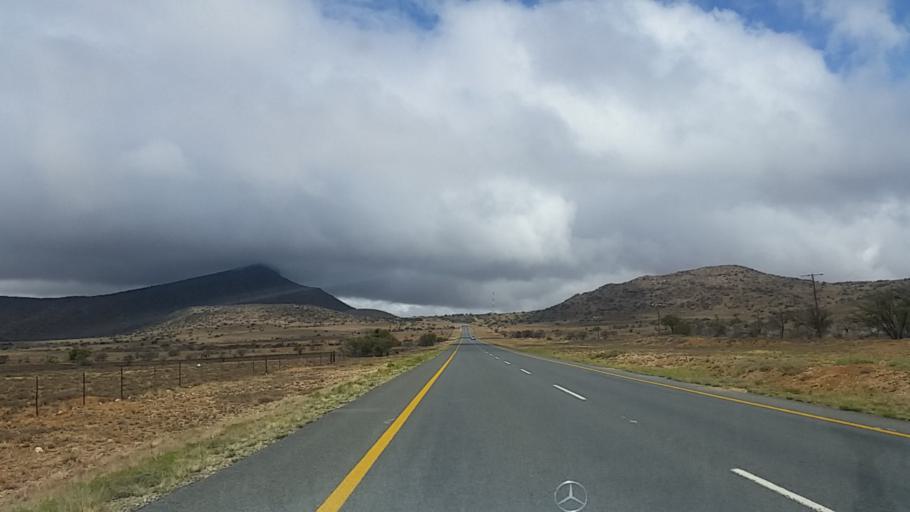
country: ZA
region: Eastern Cape
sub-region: Cacadu District Municipality
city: Graaff-Reinet
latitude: -32.0954
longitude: 24.6044
